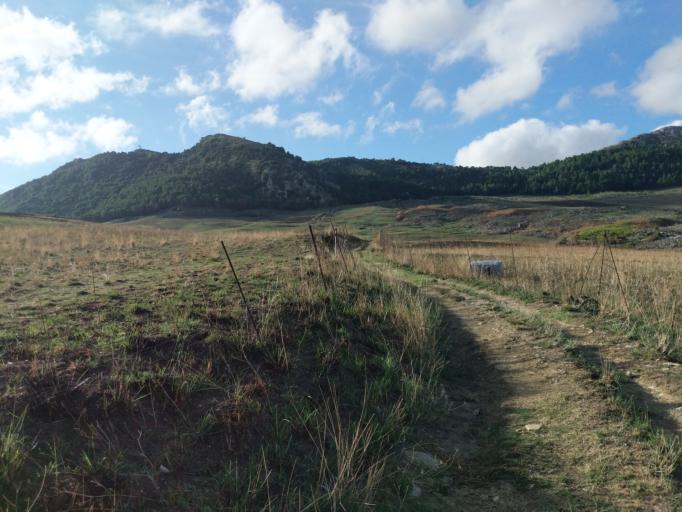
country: IT
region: Sicily
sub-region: Palermo
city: Santa Cristina Gela
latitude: 37.9716
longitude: 13.3341
